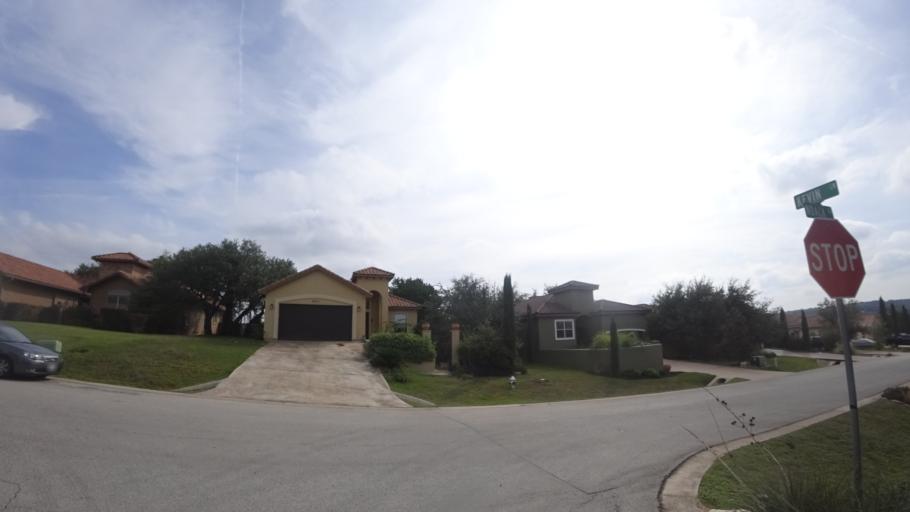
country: US
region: Texas
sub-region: Travis County
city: Hudson Bend
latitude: 30.3869
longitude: -97.9295
